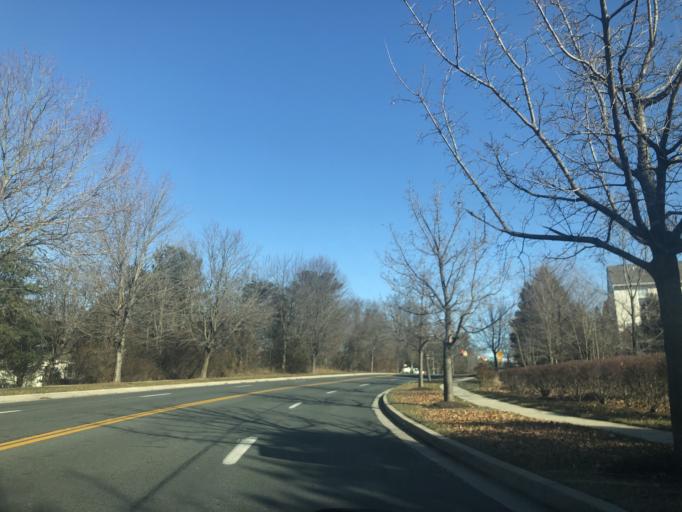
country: US
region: Maryland
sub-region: Howard County
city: Columbia
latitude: 39.2043
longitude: -76.8341
